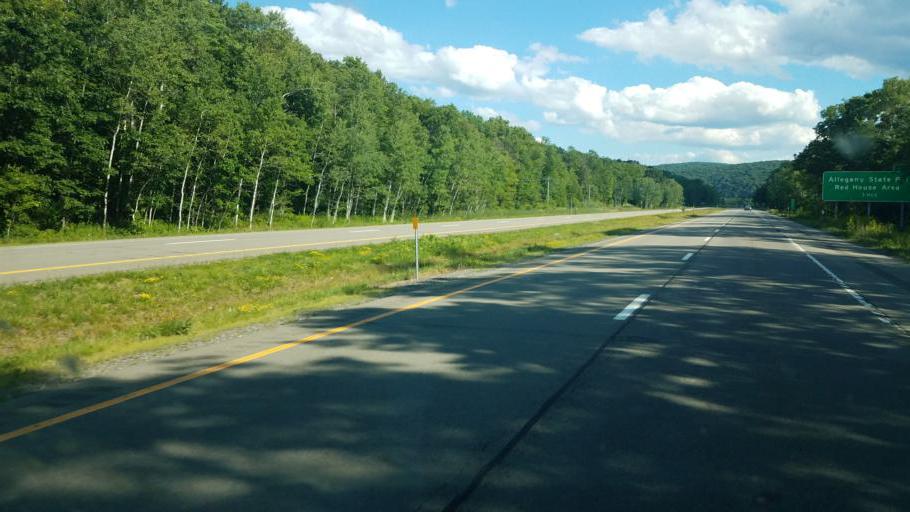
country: US
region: New York
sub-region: Cattaraugus County
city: Salamanca
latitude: 42.1240
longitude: -78.7789
